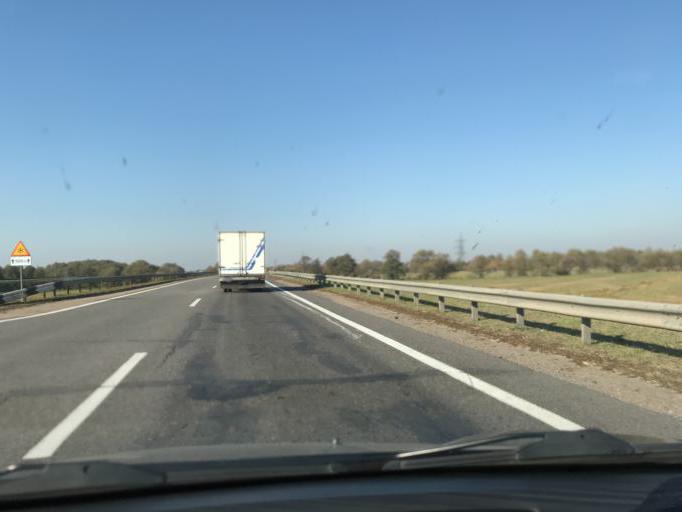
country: BY
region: Minsk
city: Dukora
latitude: 53.6618
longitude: 27.9443
